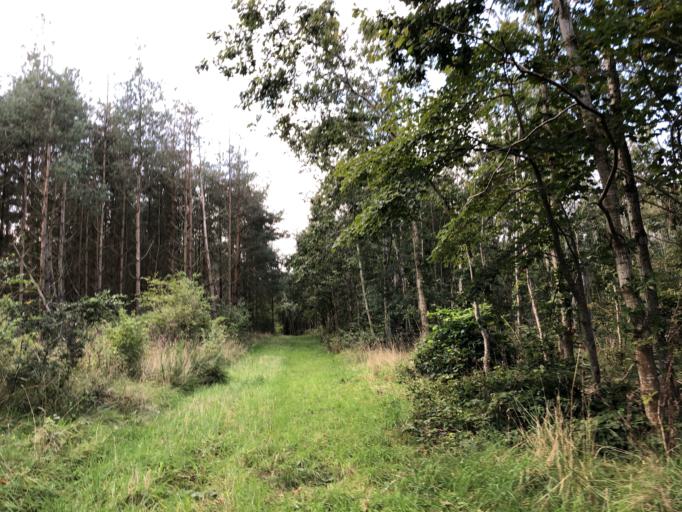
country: DK
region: Central Jutland
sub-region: Holstebro Kommune
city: Ulfborg
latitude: 56.3724
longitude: 8.3407
